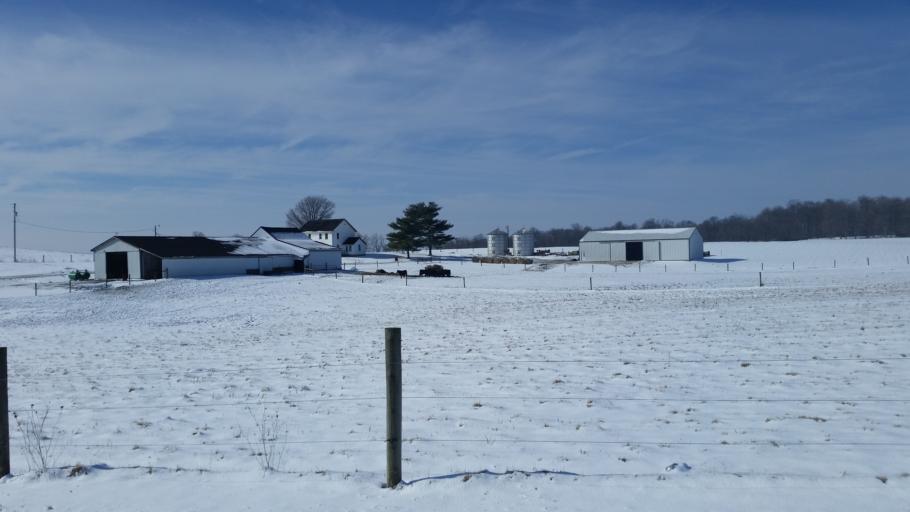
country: US
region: Ohio
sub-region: Knox County
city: Fredericktown
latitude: 40.5085
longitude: -82.6850
